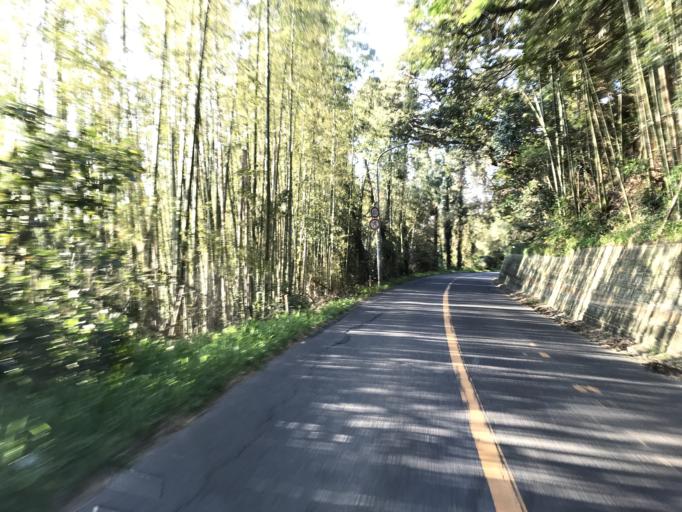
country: JP
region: Chiba
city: Yokaichiba
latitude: 35.7206
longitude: 140.5635
